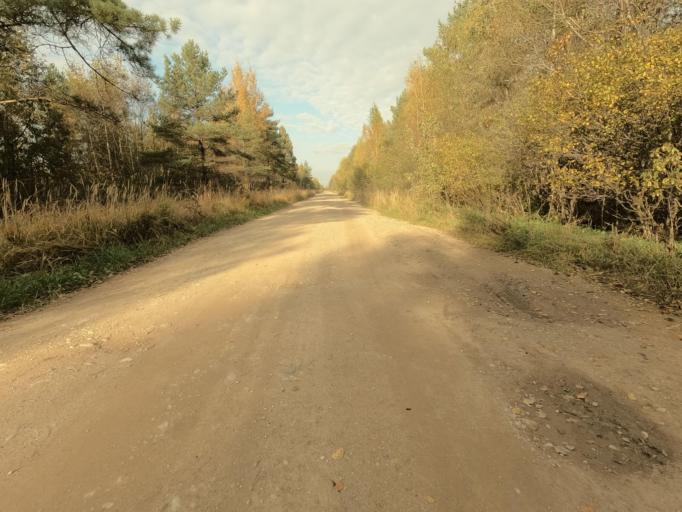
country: RU
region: Novgorod
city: Volkhovskiy
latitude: 58.8996
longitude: 31.0324
